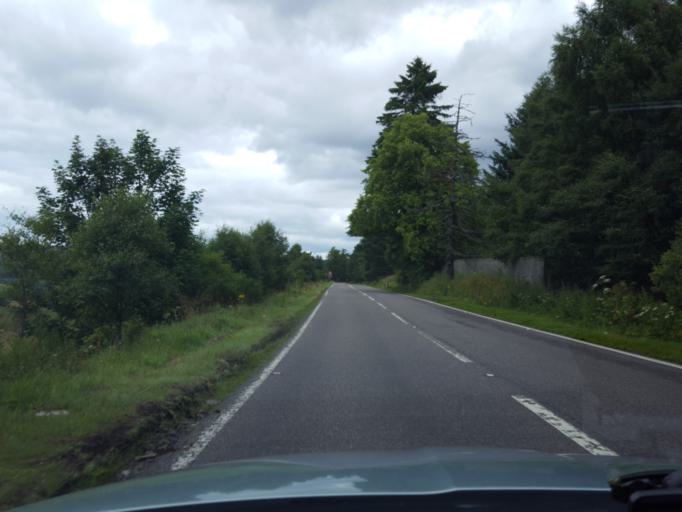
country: GB
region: Scotland
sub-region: Highland
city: Grantown on Spey
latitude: 57.3853
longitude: -3.4640
